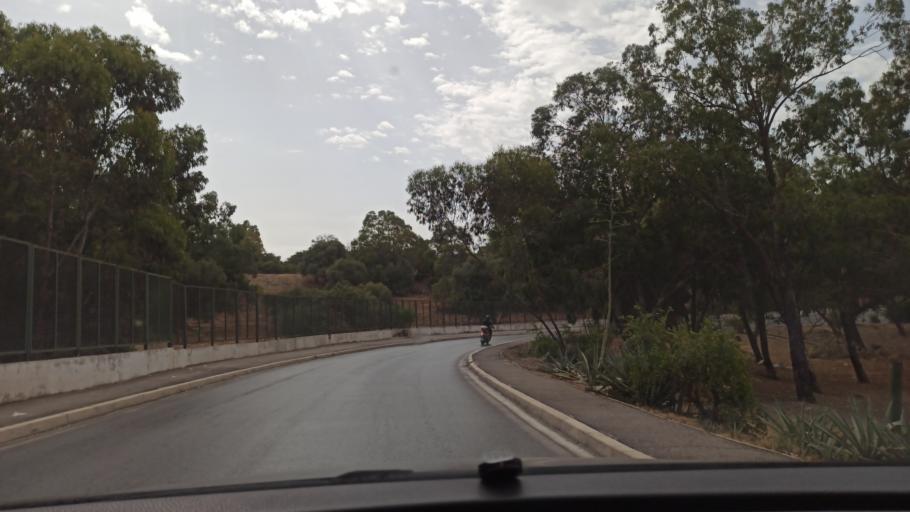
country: TN
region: Tunis
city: Tunis
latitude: 36.8255
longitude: 10.1688
